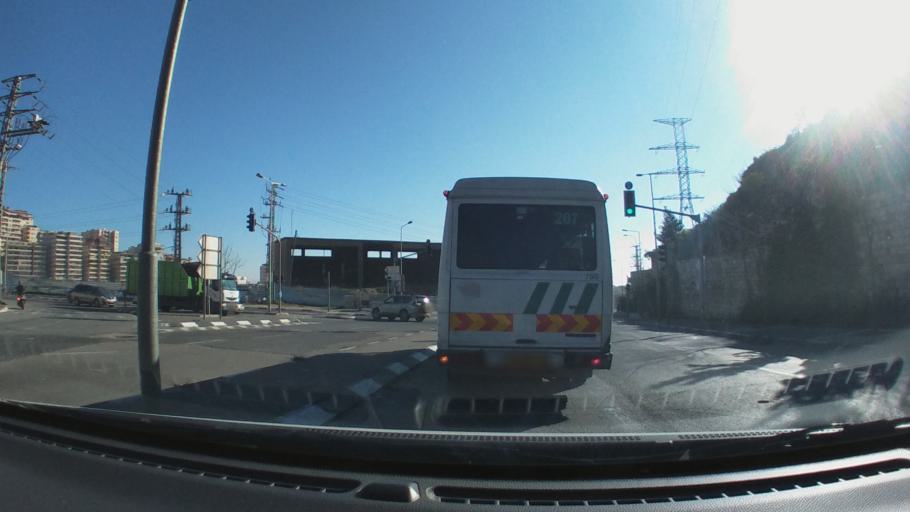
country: PS
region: West Bank
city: `Anata
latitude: 31.8082
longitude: 35.2393
